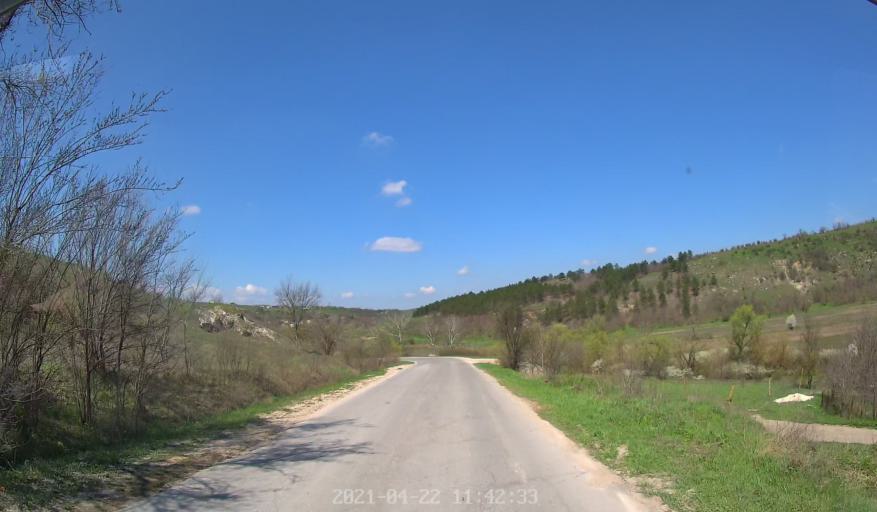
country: MD
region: Chisinau
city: Ciorescu
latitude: 47.1366
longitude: 28.9079
